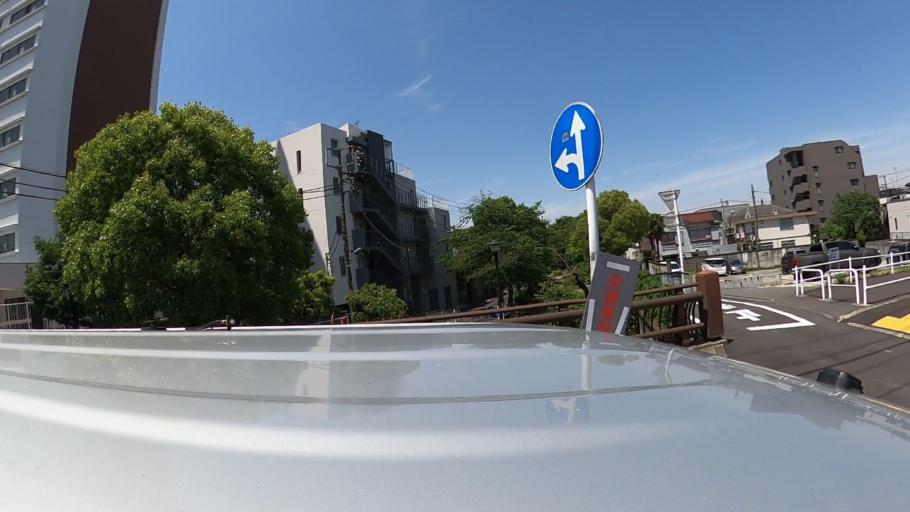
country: JP
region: Kanagawa
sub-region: Kawasaki-shi
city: Kawasaki
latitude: 35.5657
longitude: 139.7363
